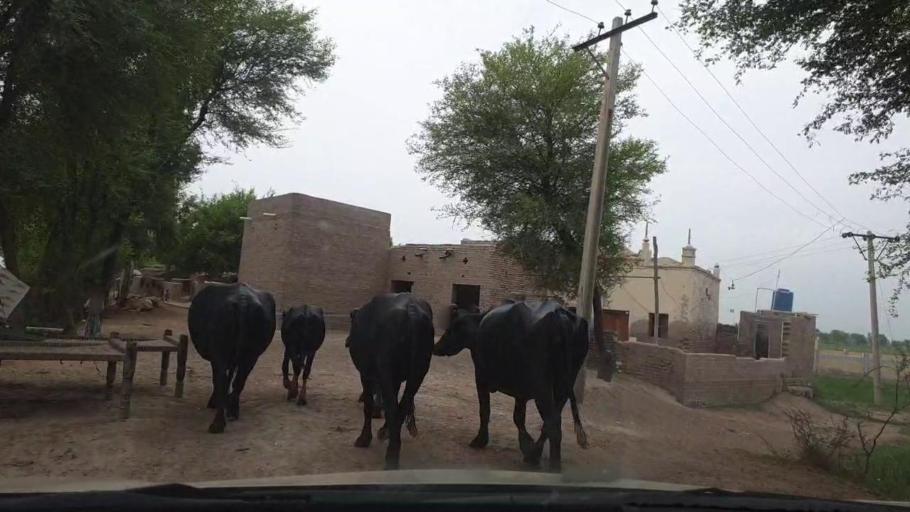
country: PK
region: Sindh
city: Ratodero
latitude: 27.7567
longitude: 68.3085
